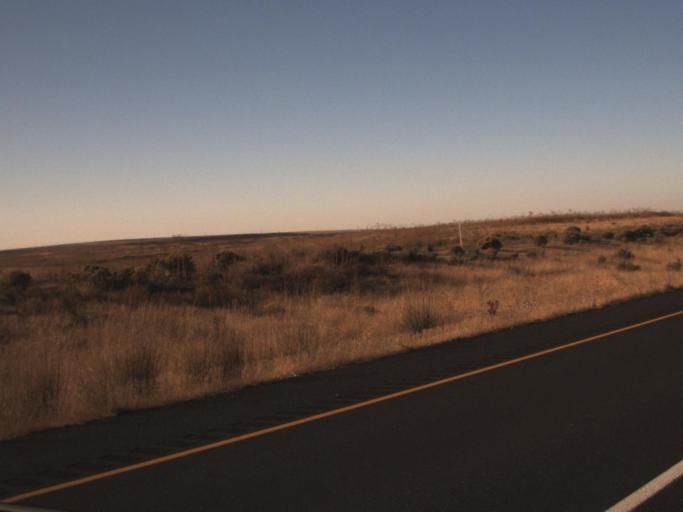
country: US
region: Washington
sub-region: Franklin County
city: Connell
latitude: 46.6121
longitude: -118.9112
